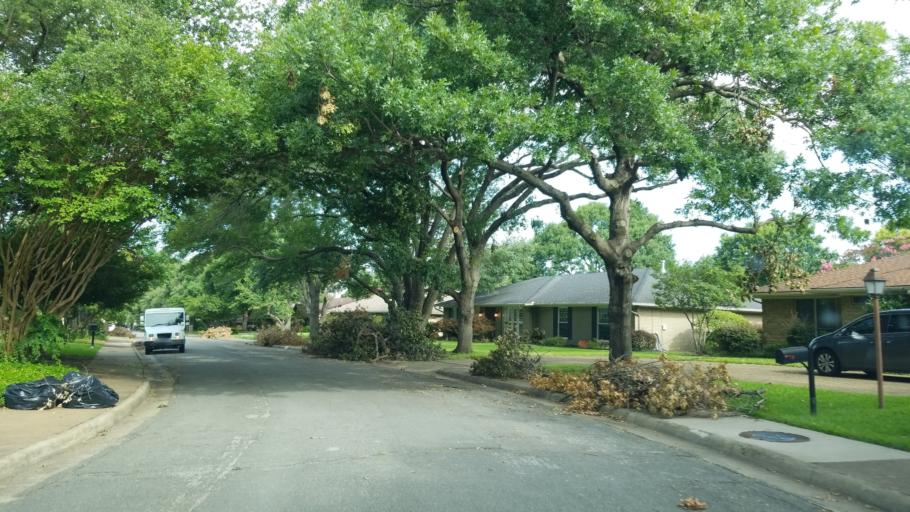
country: US
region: Texas
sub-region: Dallas County
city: Farmers Branch
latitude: 32.8932
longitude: -96.8474
